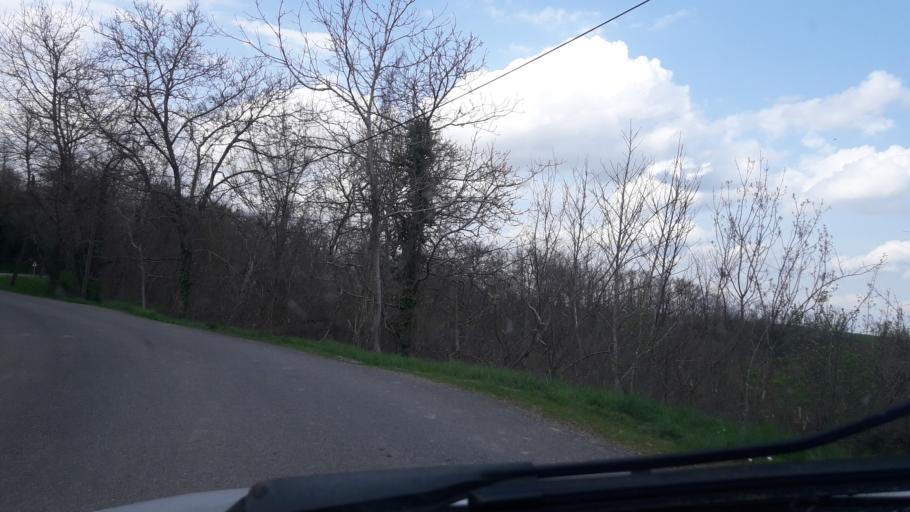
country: FR
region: Midi-Pyrenees
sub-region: Departement de l'Ariege
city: Lezat-sur-Leze
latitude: 43.1889
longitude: 1.3319
